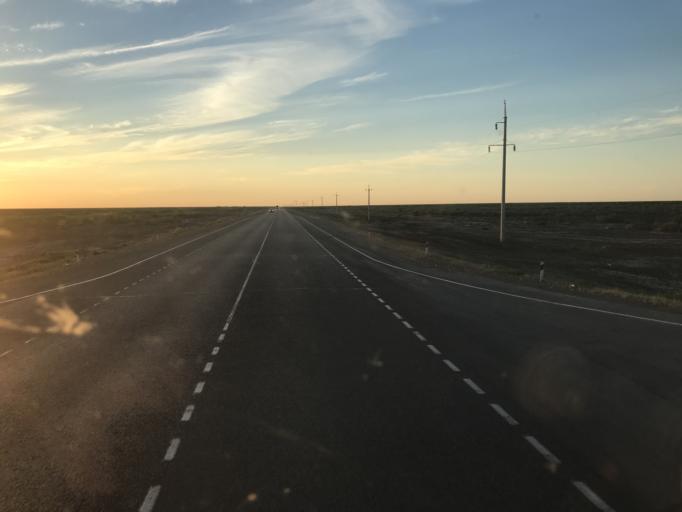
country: KZ
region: Qyzylorda
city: Zhosaly
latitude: 45.2456
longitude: 64.1182
